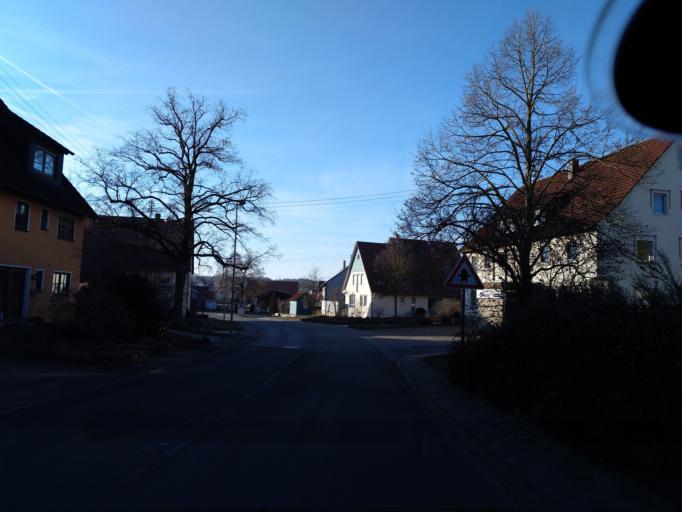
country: DE
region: Baden-Wuerttemberg
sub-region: Regierungsbezirk Stuttgart
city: Ilshofen
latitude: 49.1037
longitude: 9.9825
